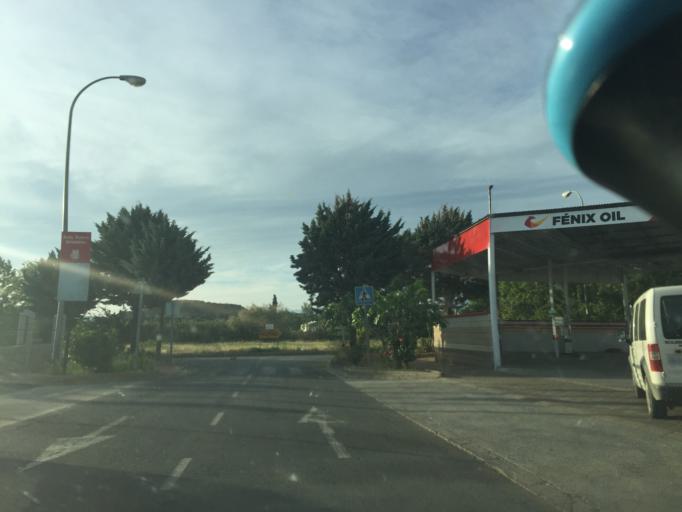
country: ES
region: Andalusia
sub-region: Provincia de Granada
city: Guadix
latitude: 37.3098
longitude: -3.1548
